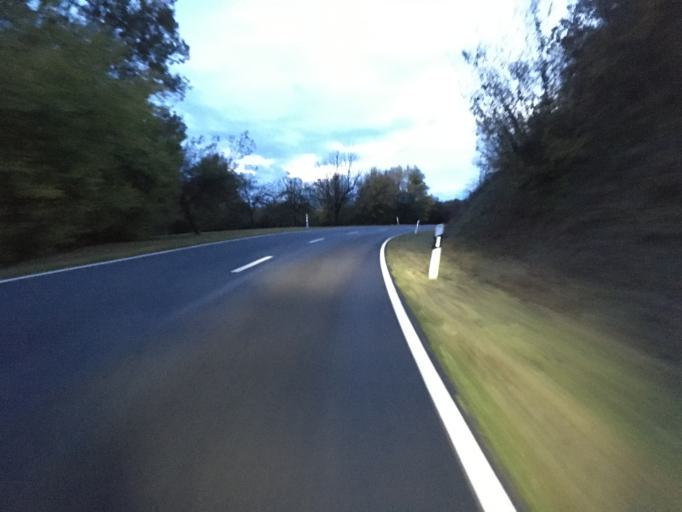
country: DE
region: Baden-Wuerttemberg
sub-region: Karlsruhe Region
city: Adelsheim
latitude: 49.3645
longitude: 9.4035
